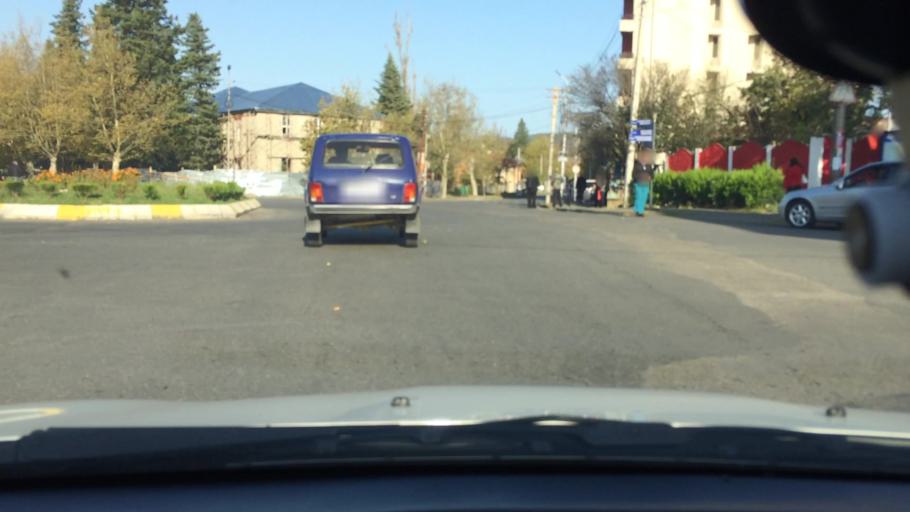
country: GE
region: Imereti
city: Kutaisi
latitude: 42.2660
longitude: 42.7186
